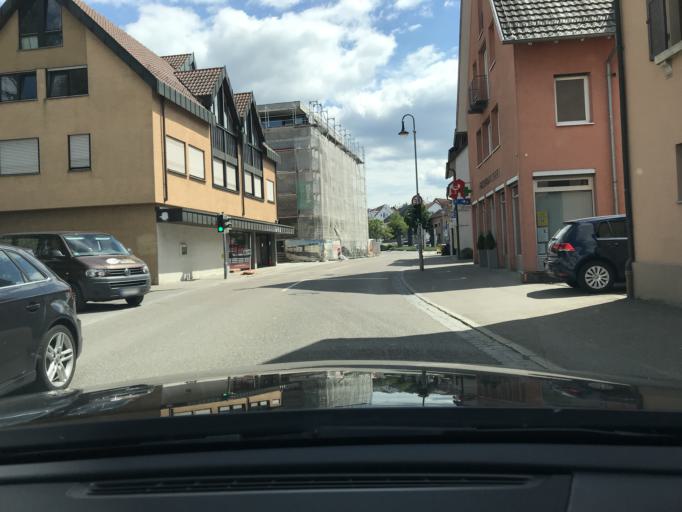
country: DE
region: Baden-Wuerttemberg
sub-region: Regierungsbezirk Stuttgart
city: Schwaikheim
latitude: 48.8756
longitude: 9.3512
